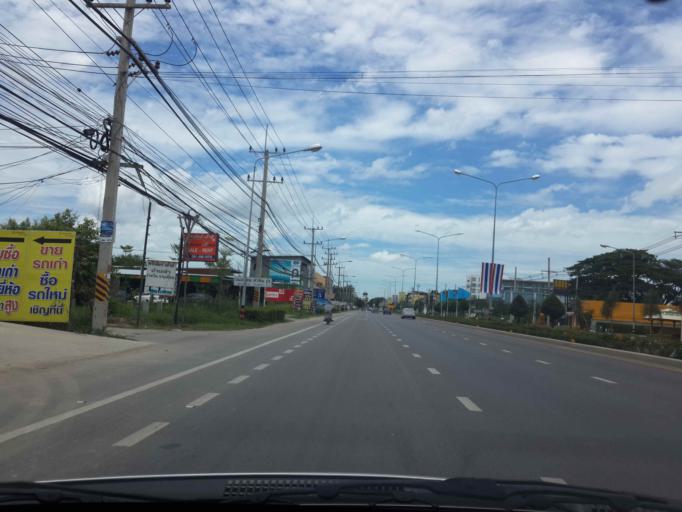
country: TH
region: Prachuap Khiri Khan
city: Hua Hin
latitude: 12.6222
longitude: 99.9506
